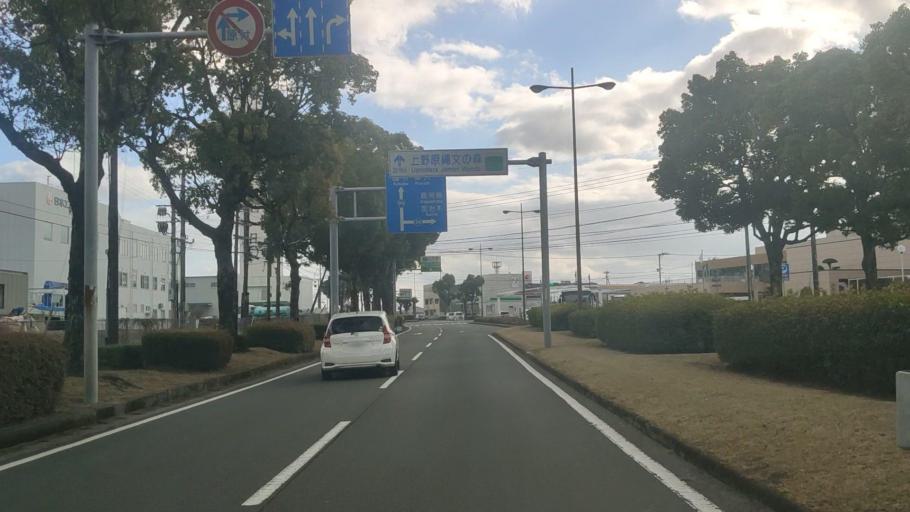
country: JP
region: Kagoshima
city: Kokubu-matsuki
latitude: 31.7961
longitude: 130.7177
